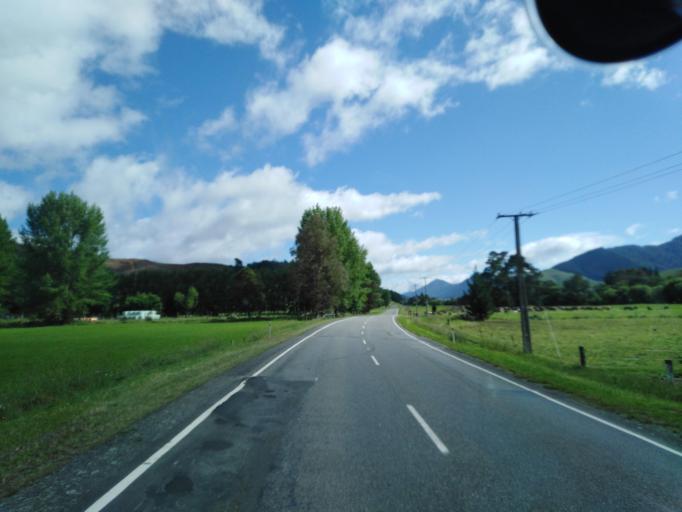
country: NZ
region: Nelson
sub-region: Nelson City
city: Nelson
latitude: -41.2675
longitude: 173.5725
